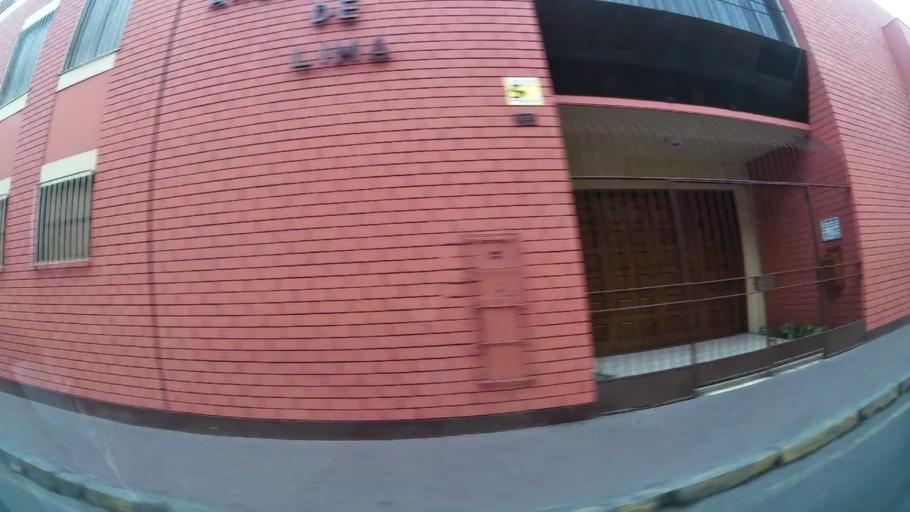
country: PE
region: Lima
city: Lima
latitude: -12.0427
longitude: -77.0362
